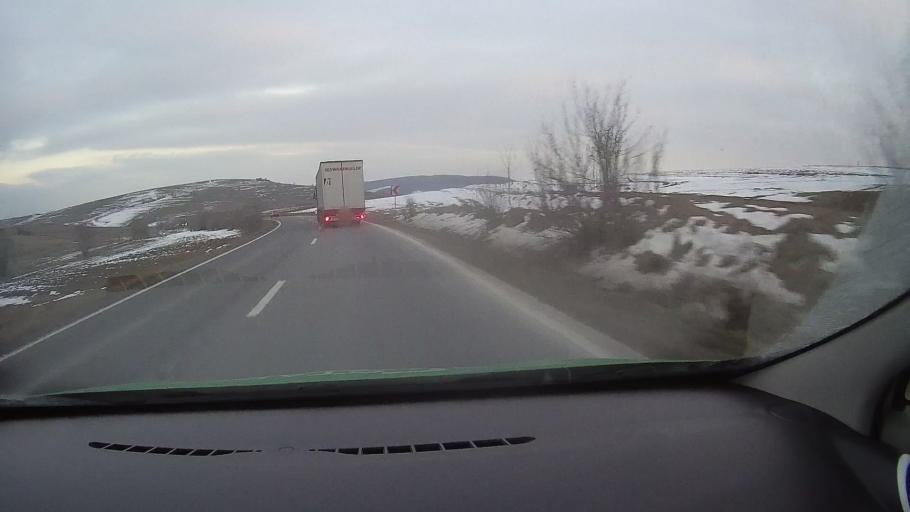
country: RO
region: Harghita
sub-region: Comuna Lupeni
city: Lupeni
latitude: 46.3512
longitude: 25.2574
